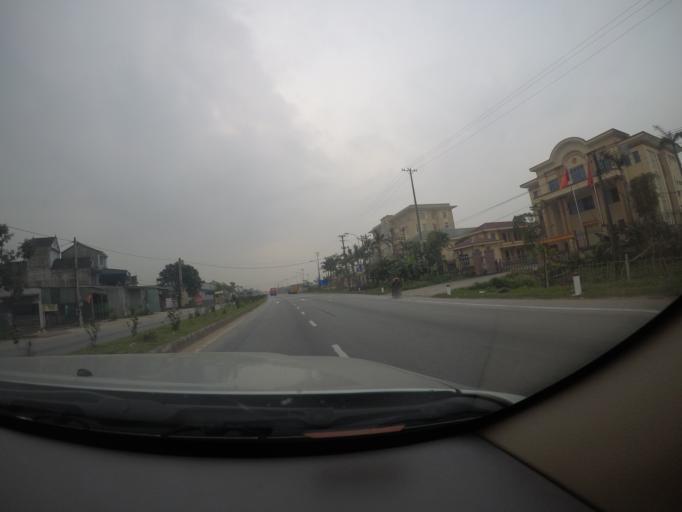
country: VN
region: Ha Tinh
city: Cam Xuyen
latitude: 18.2567
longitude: 105.9907
